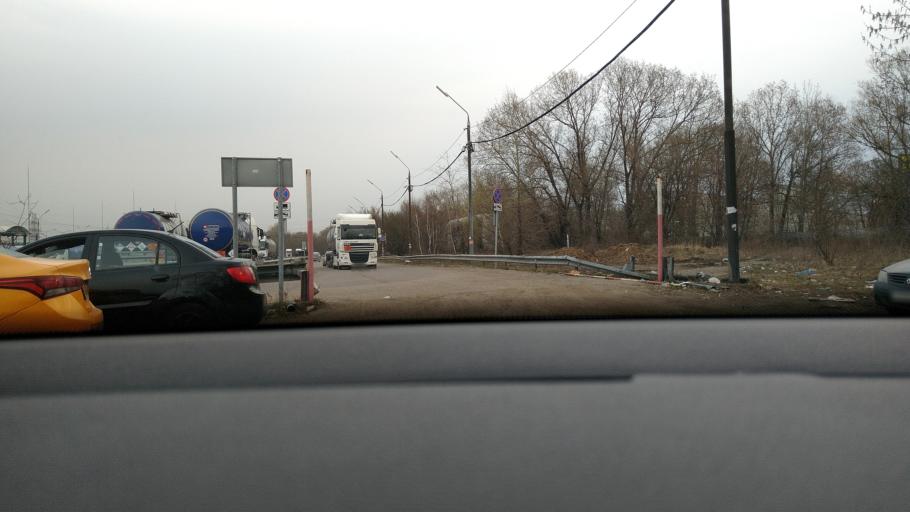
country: RU
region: Moskovskaya
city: Kotel'niki
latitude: 55.6442
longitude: 37.8226
